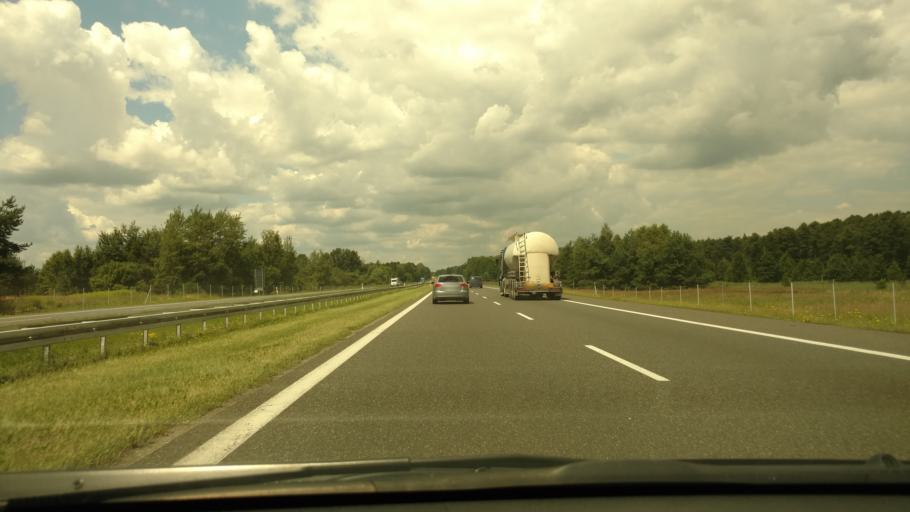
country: PL
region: Lesser Poland Voivodeship
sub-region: Powiat chrzanowski
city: Bolecin
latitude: 50.1228
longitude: 19.4915
